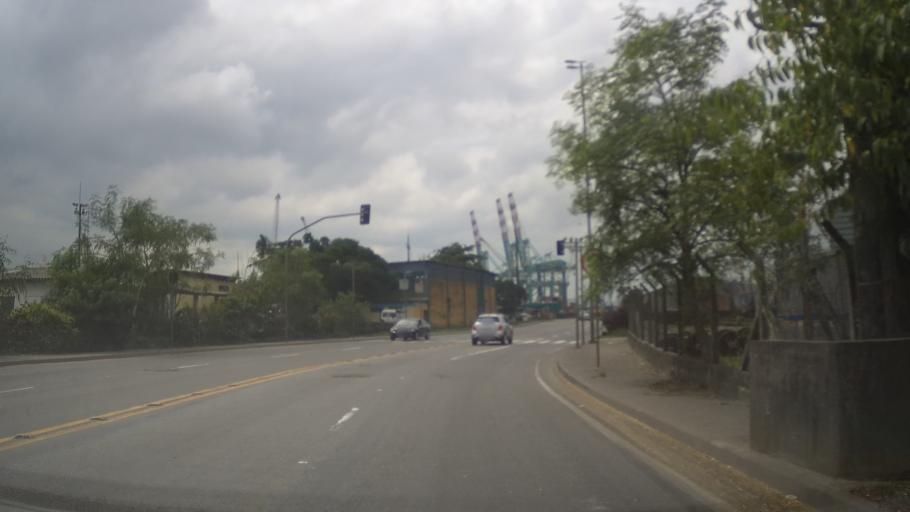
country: BR
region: Sao Paulo
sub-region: Santos
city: Santos
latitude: -23.9277
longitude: -46.3411
